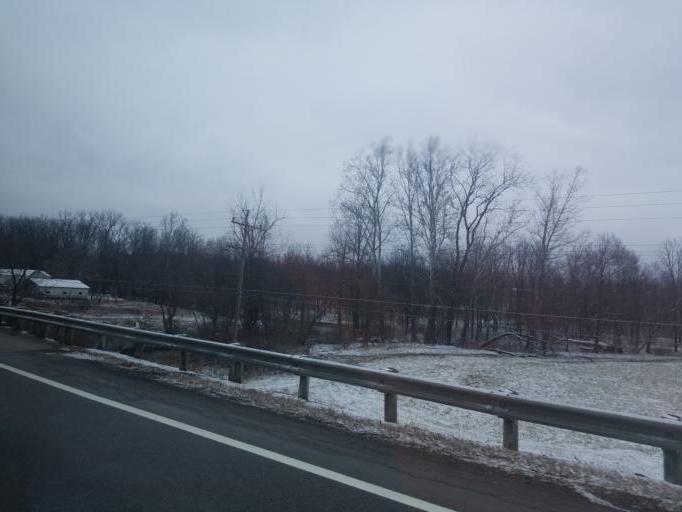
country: US
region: Ohio
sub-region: Licking County
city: Johnstown
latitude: 40.1632
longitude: -82.6941
